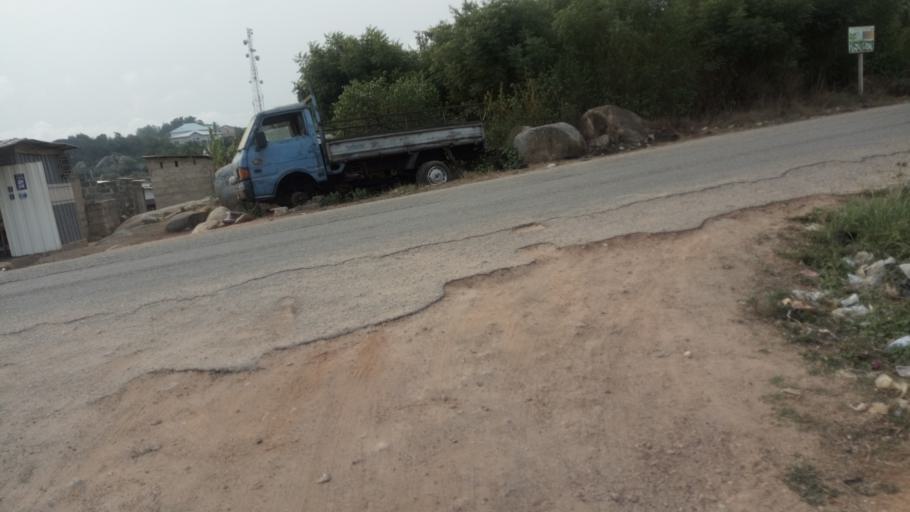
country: GH
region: Central
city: Winneba
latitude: 5.3570
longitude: -0.6243
